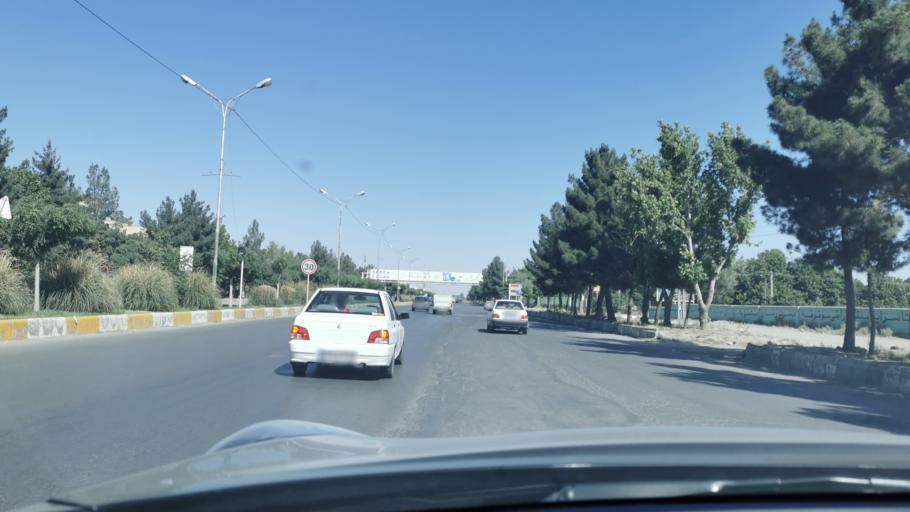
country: IR
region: Razavi Khorasan
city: Chenaran
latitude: 36.6370
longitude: 59.1253
